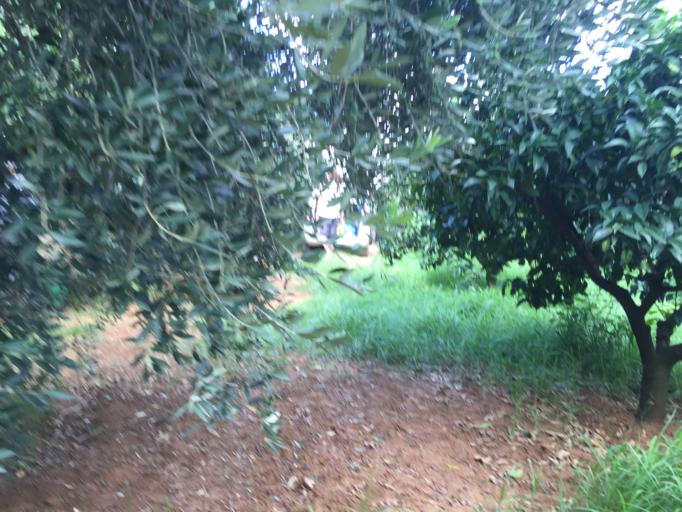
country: IT
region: Basilicate
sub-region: Provincia di Matera
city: Policoro
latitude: 40.2067
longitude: 16.6156
